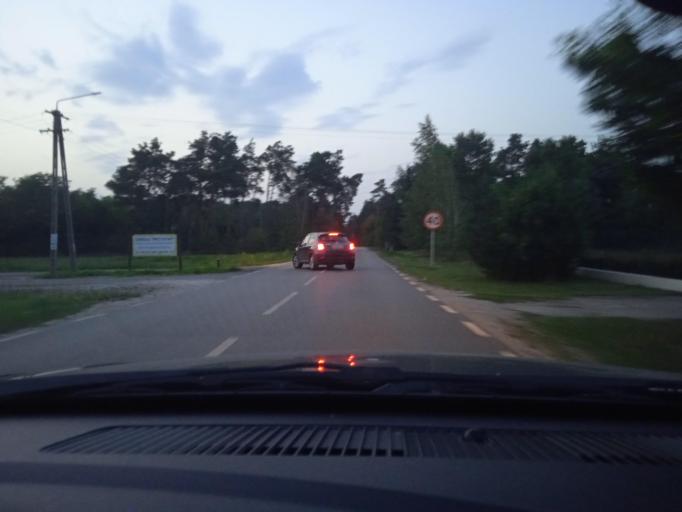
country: PL
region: Masovian Voivodeship
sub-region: Powiat nowodworski
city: Pomiechowek
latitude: 52.5391
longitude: 20.6805
